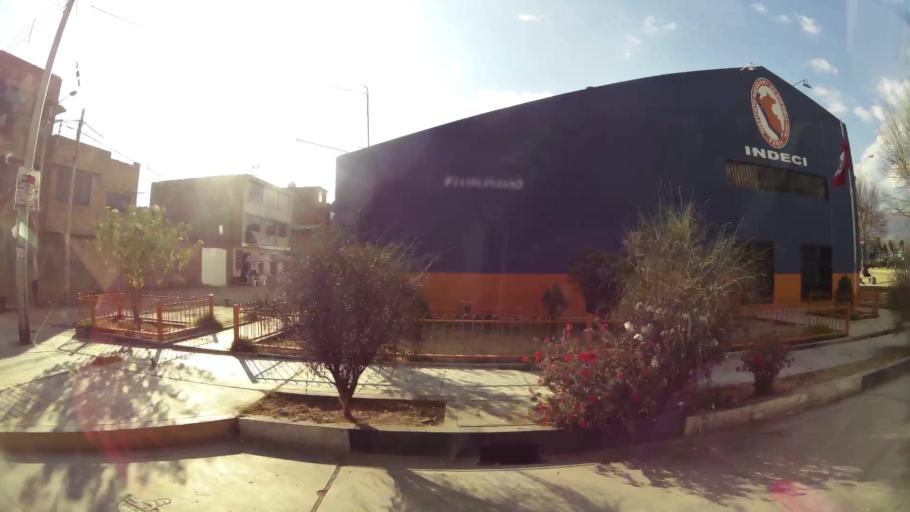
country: PE
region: Junin
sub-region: Provincia de Huancayo
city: El Tambo
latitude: -12.0480
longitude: -75.2174
